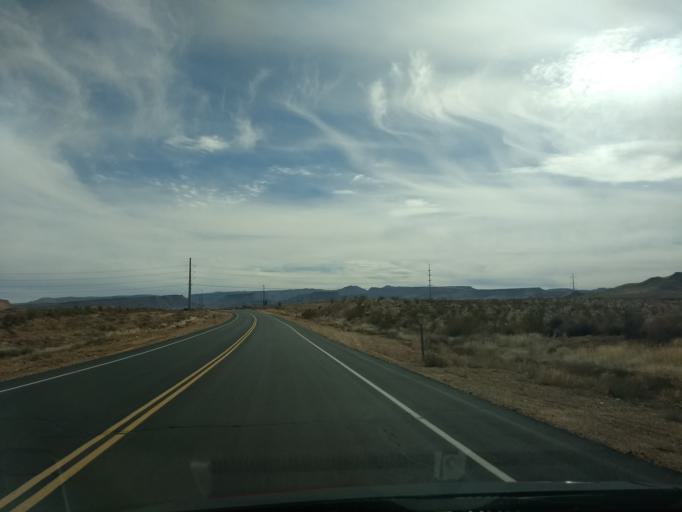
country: US
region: Utah
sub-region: Washington County
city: Washington
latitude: 37.0169
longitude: -113.4983
